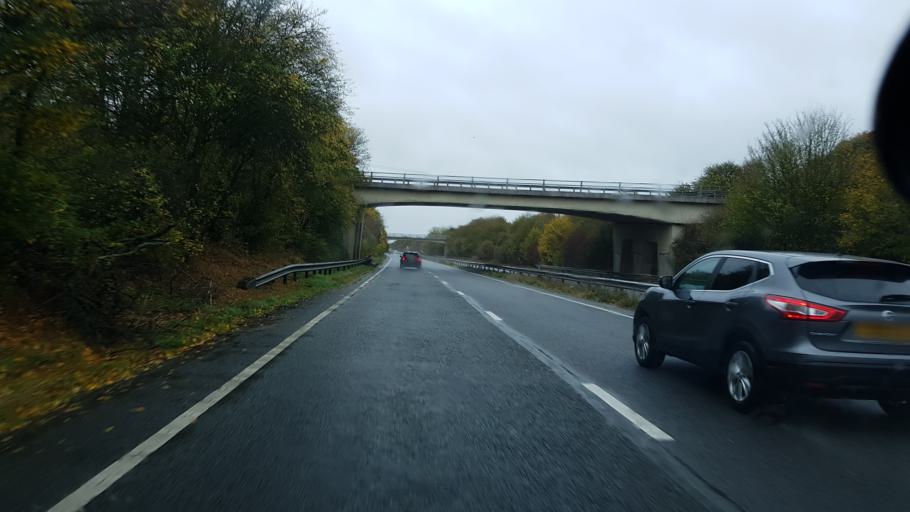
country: GB
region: England
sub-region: Oxfordshire
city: Witney
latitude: 51.7775
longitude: -1.5129
